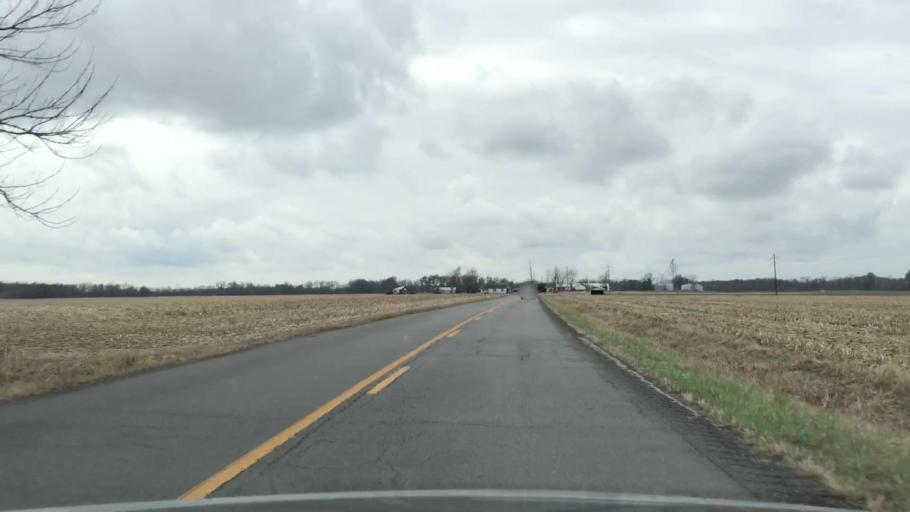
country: US
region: Kentucky
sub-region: McLean County
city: Calhoun
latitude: 37.5264
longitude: -87.3343
